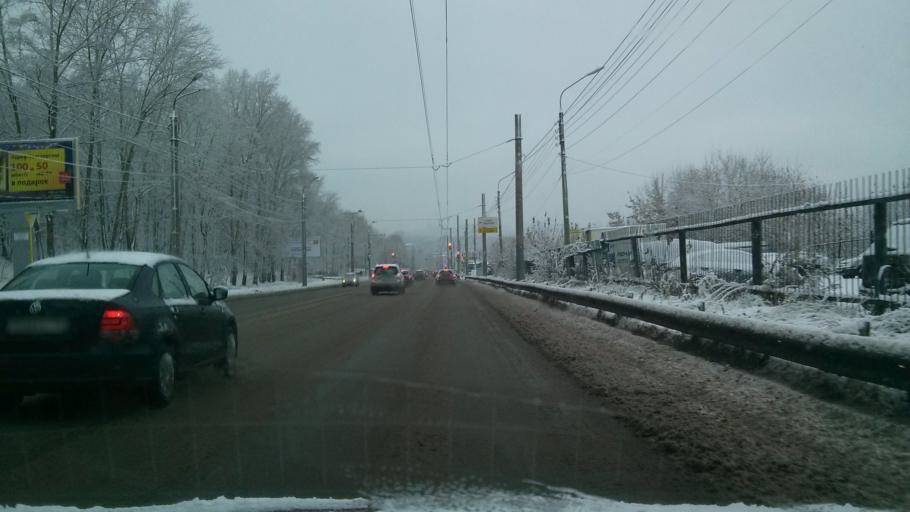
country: RU
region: Nizjnij Novgorod
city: Afonino
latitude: 56.2995
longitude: 44.0726
